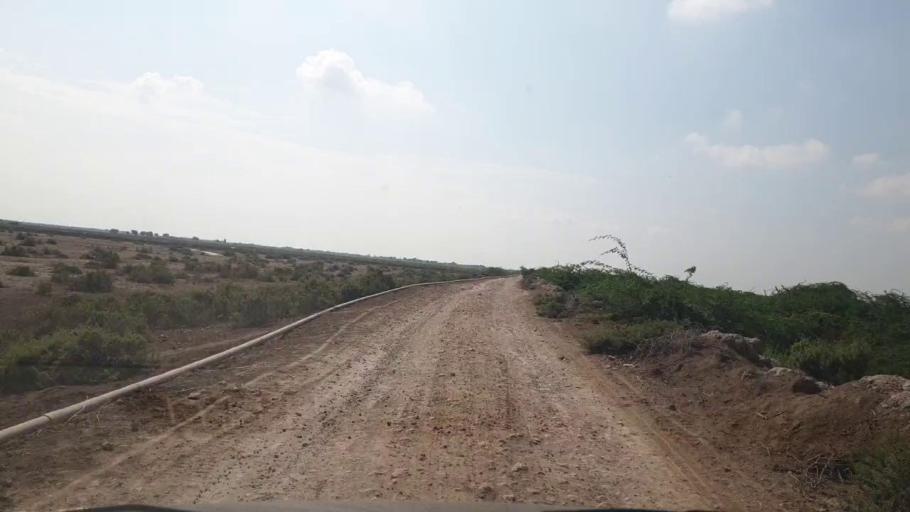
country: PK
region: Sindh
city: Badin
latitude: 24.5029
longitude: 68.6080
